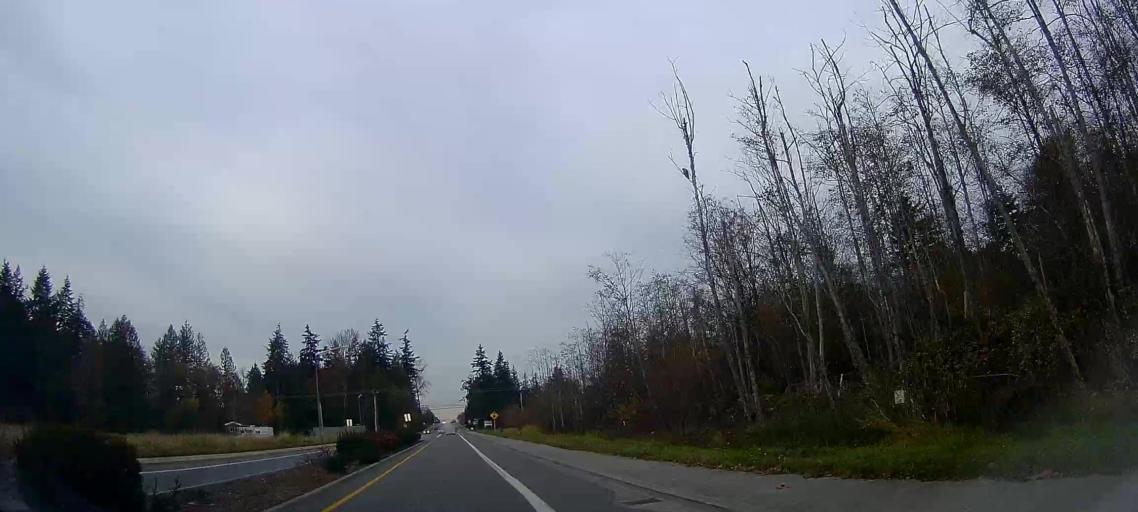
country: US
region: Washington
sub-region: Skagit County
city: Mount Vernon
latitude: 48.4052
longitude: -122.3133
